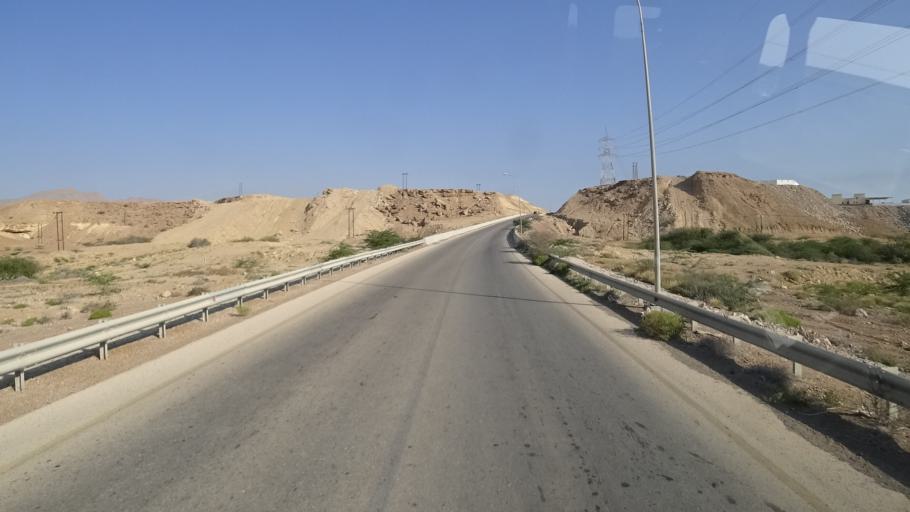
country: OM
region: Ash Sharqiyah
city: Sur
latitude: 22.5838
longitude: 59.4571
